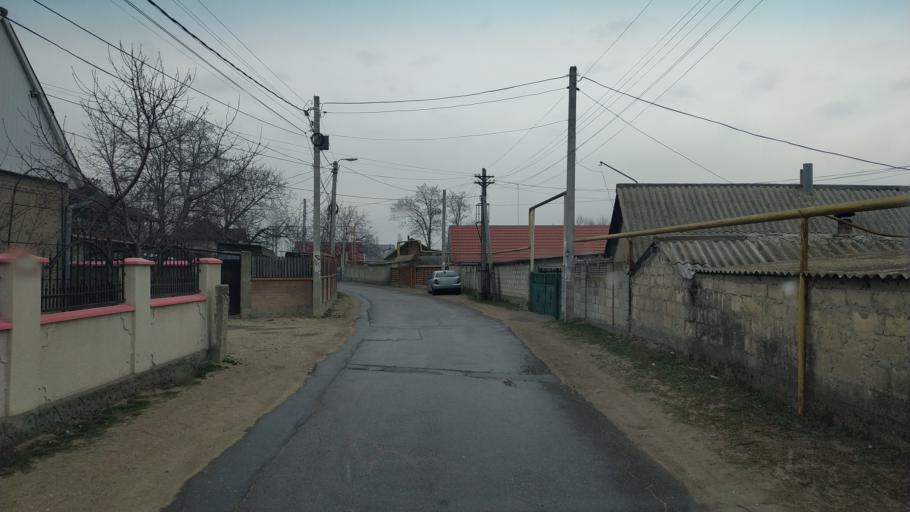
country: MD
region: Chisinau
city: Singera
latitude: 46.9140
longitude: 28.9700
